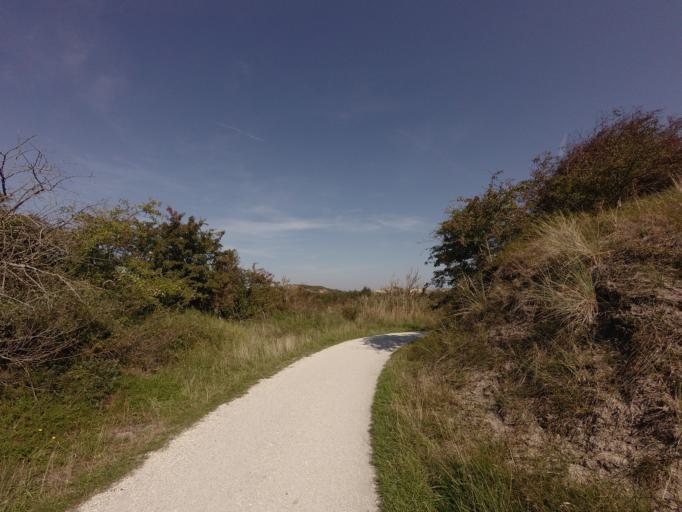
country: NL
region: Friesland
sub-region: Gemeente Schiermonnikoog
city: Schiermonnikoog
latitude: 53.4793
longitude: 6.1440
